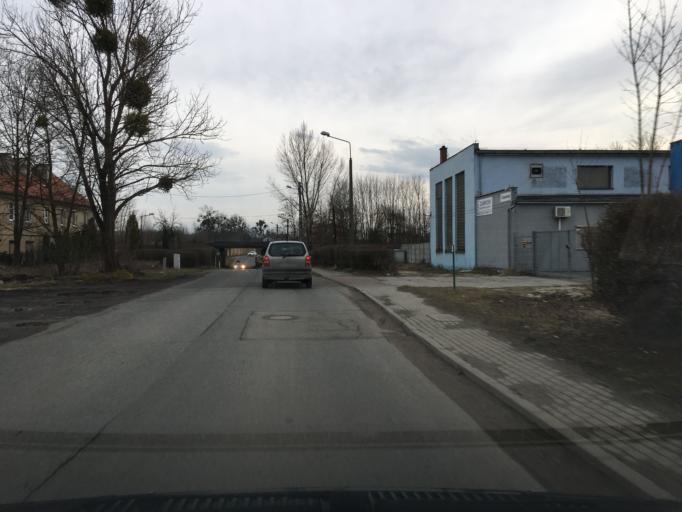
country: PL
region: Opole Voivodeship
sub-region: Powiat kedzierzynsko-kozielski
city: Kozle
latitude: 50.3496
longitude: 18.1417
